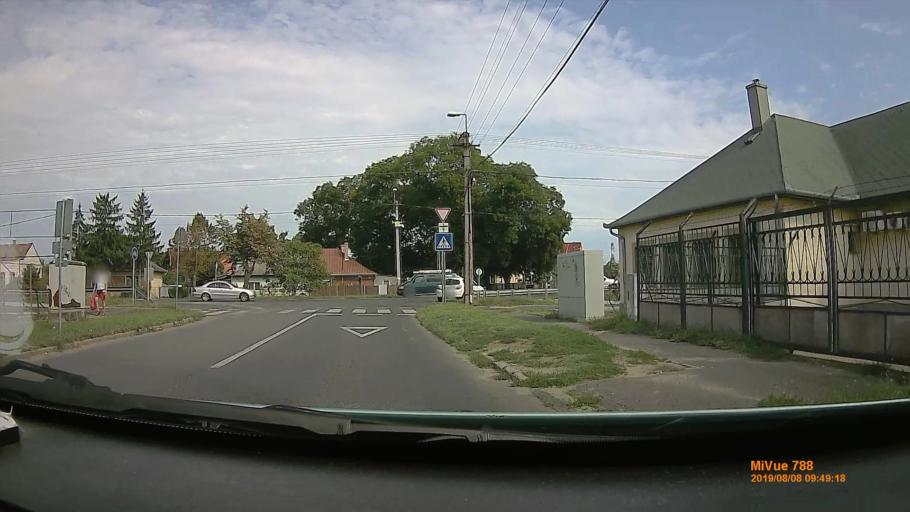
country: HU
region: Hajdu-Bihar
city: Debrecen
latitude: 47.5463
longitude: 21.6530
